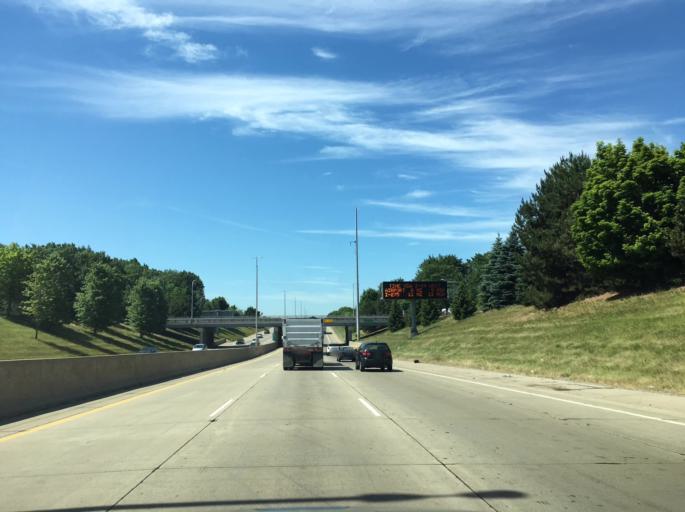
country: US
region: Michigan
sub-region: Wayne County
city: Allen Park
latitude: 42.2855
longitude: -83.2107
